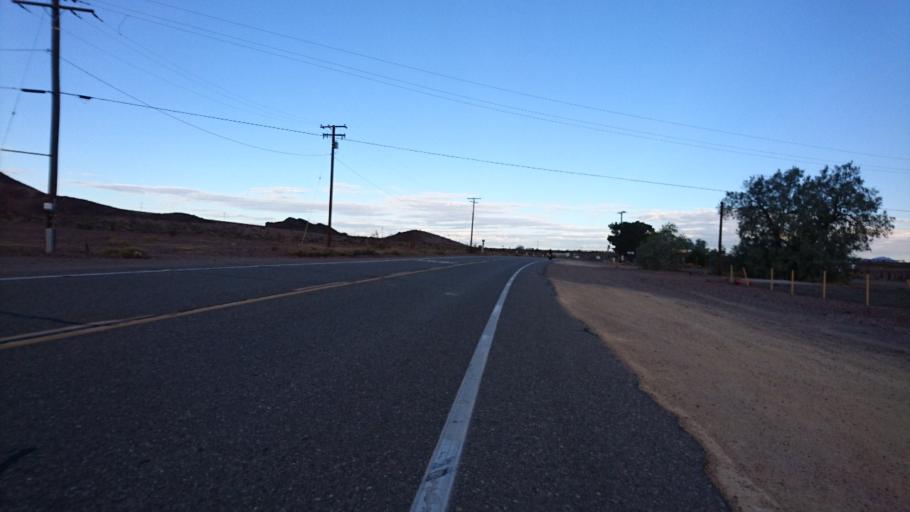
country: US
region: California
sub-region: San Bernardino County
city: Barstow
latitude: 34.8276
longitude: -116.6912
